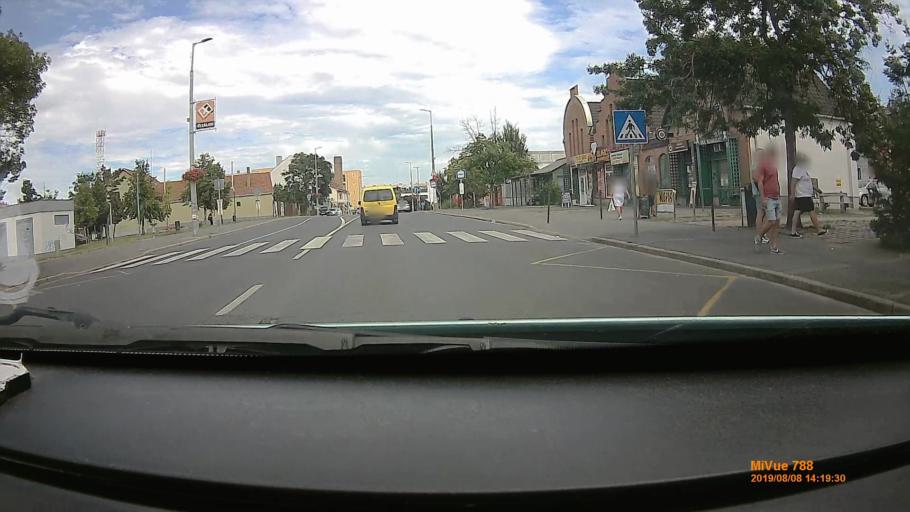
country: HU
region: Szabolcs-Szatmar-Bereg
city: Mateszalka
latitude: 47.9531
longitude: 22.3199
